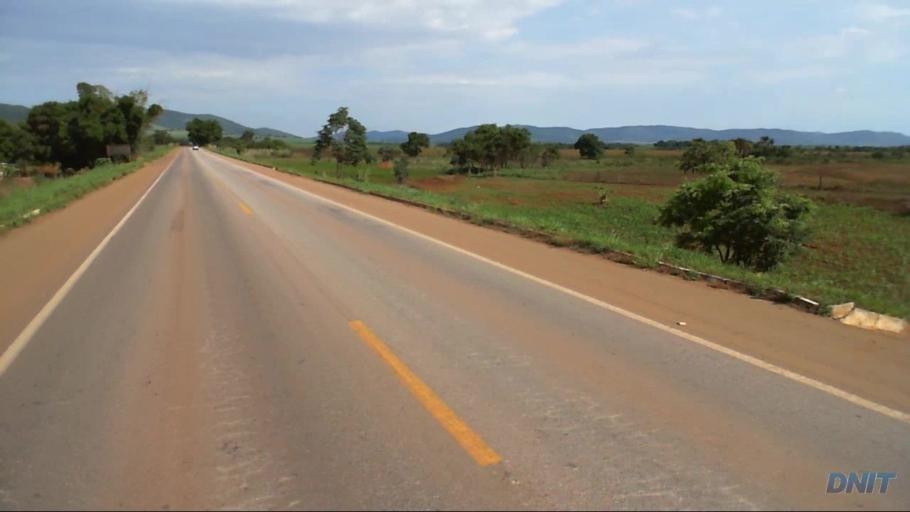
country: BR
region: Goias
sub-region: Barro Alto
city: Barro Alto
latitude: -15.0625
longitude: -48.8758
